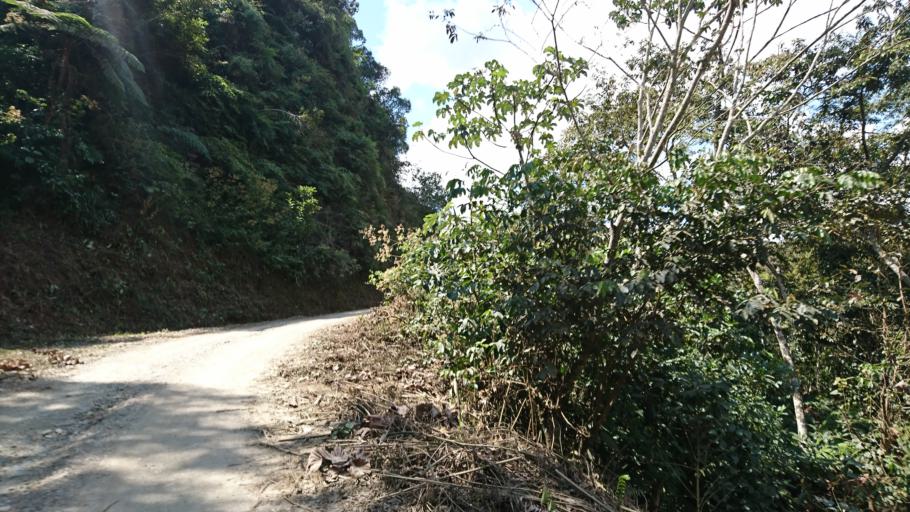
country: BO
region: La Paz
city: Coroico
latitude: -16.0791
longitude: -67.7933
